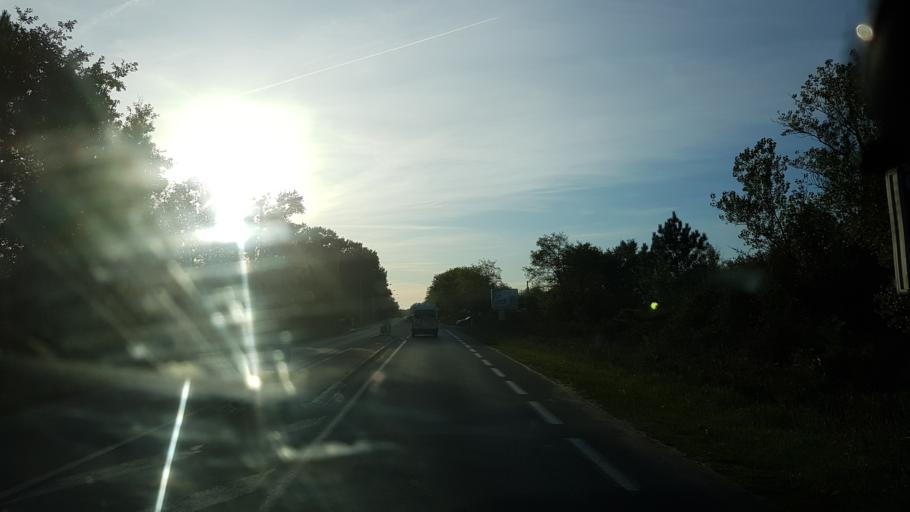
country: FR
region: Aquitaine
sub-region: Departement de la Gironde
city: Saint-Medard-en-Jalles
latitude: 44.8460
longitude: -0.7240
